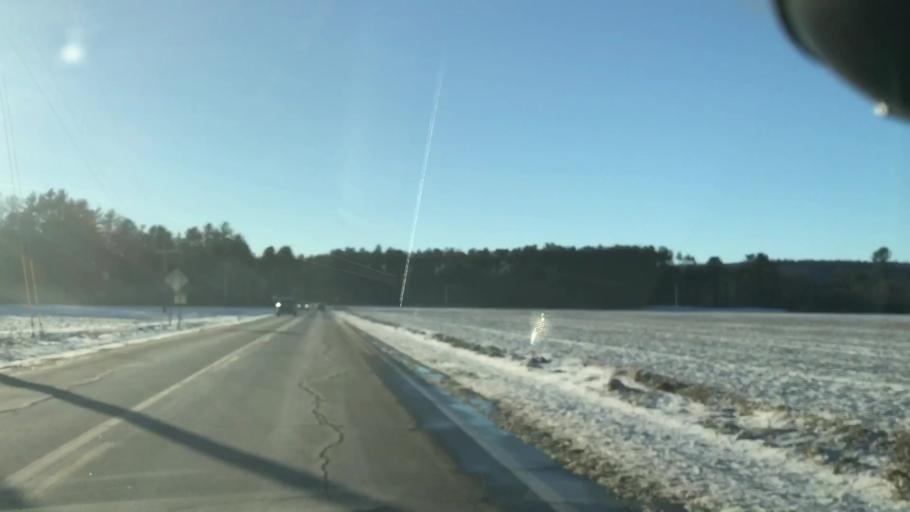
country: US
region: New Hampshire
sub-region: Grafton County
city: North Haverhill
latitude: 44.0718
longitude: -72.0336
